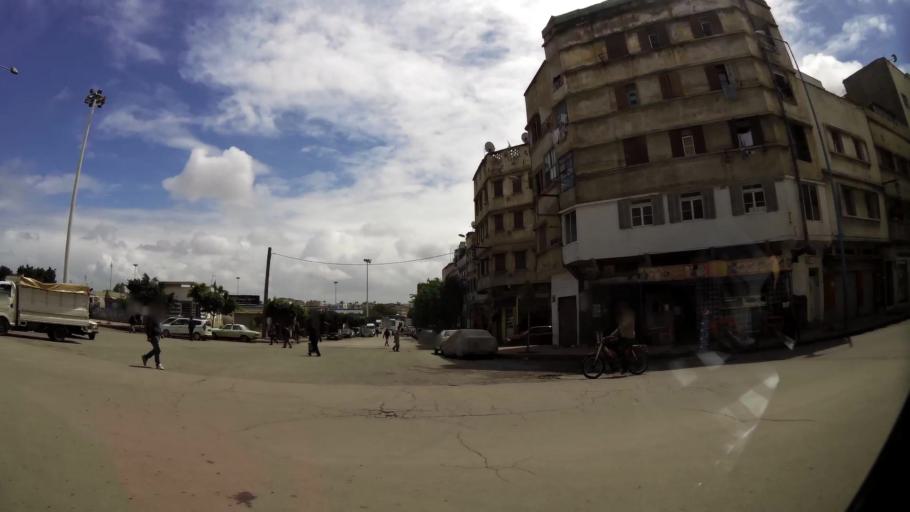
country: MA
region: Grand Casablanca
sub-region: Casablanca
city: Casablanca
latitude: 33.5755
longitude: -7.5907
